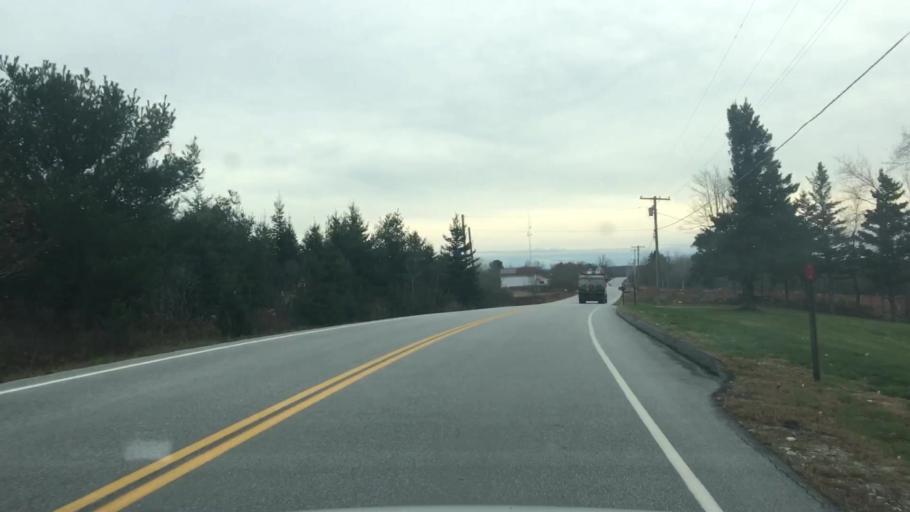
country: US
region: Maine
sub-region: Hancock County
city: Penobscot
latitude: 44.5267
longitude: -68.6660
